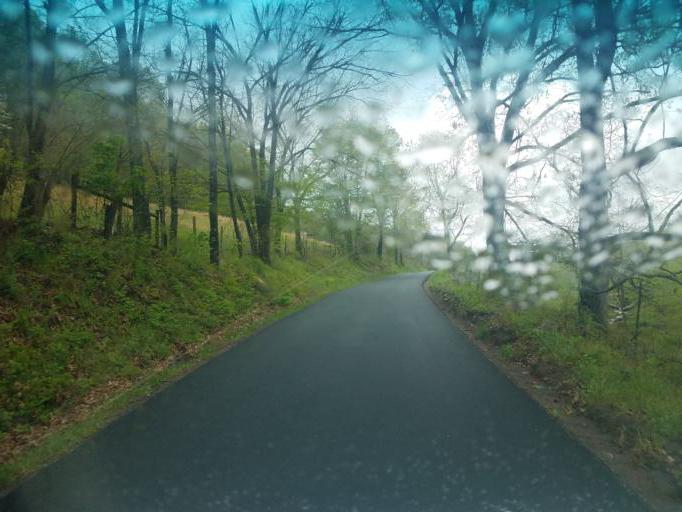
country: US
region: Virginia
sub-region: Smyth County
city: Marion
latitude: 36.9259
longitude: -81.5496
